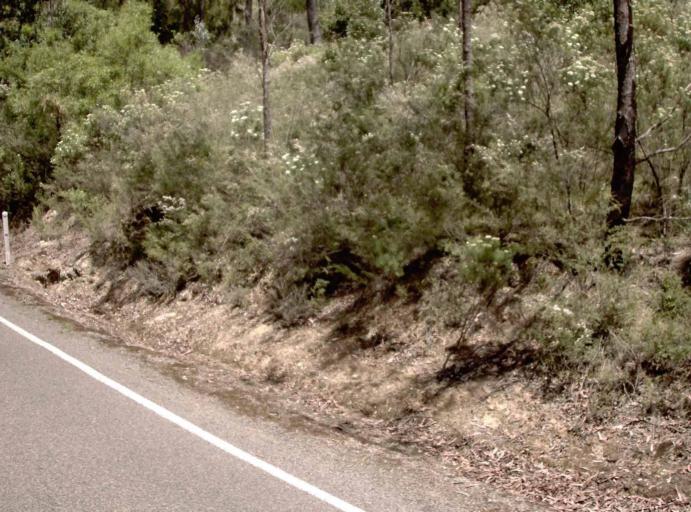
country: AU
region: Victoria
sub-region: East Gippsland
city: Lakes Entrance
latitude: -37.5821
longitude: 147.8951
